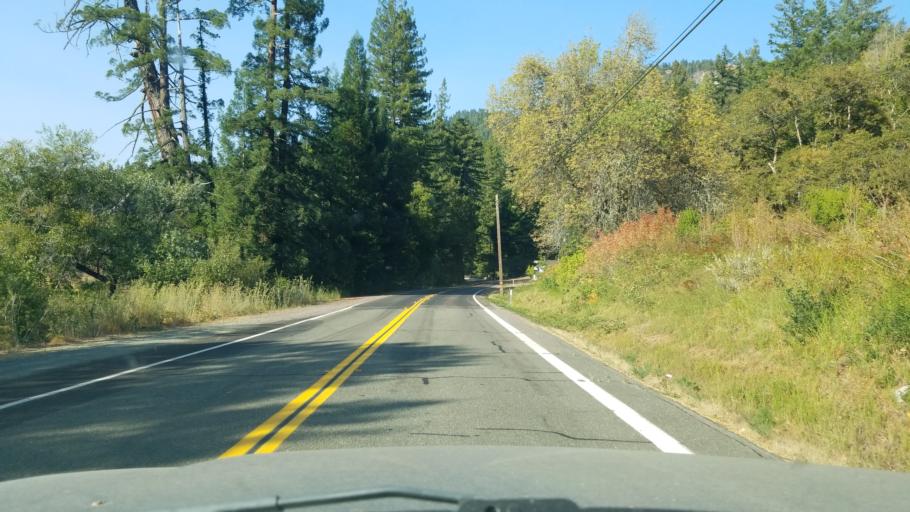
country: US
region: California
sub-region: Humboldt County
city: Redway
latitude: 40.1905
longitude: -123.7690
